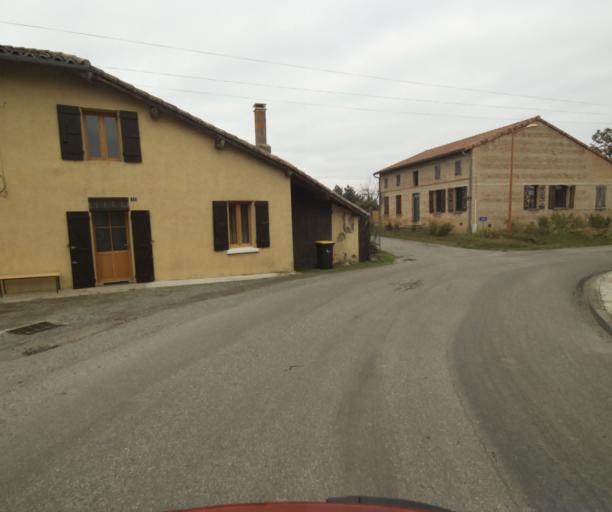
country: FR
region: Midi-Pyrenees
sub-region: Departement du Tarn-et-Garonne
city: Verdun-sur-Garonne
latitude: 43.8045
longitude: 1.2146
